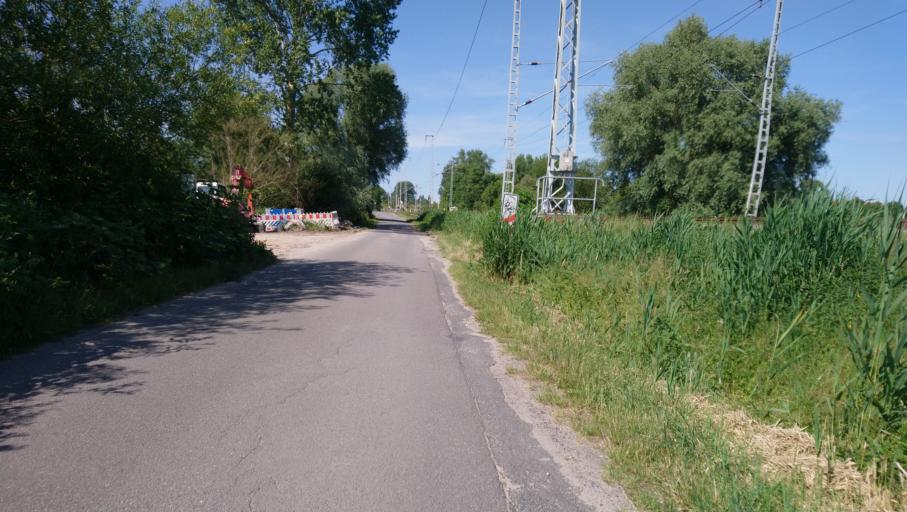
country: DE
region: Mecklenburg-Vorpommern
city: Dierkow-Neu
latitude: 54.0910
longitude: 12.1796
